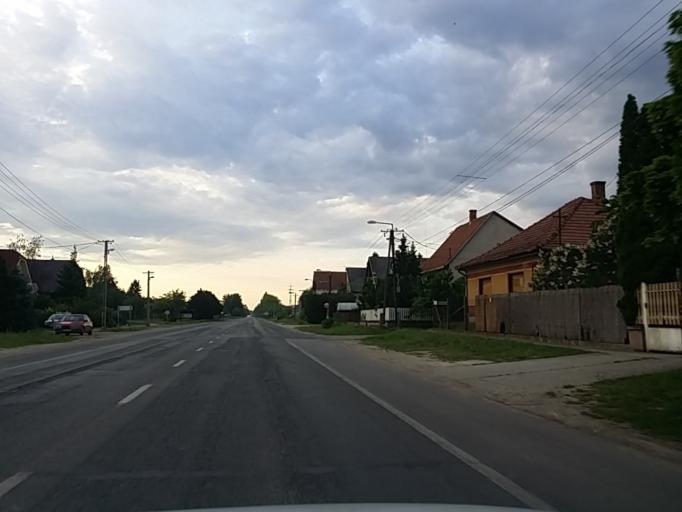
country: HU
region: Bacs-Kiskun
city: Lajosmizse
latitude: 47.0177
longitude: 19.5709
